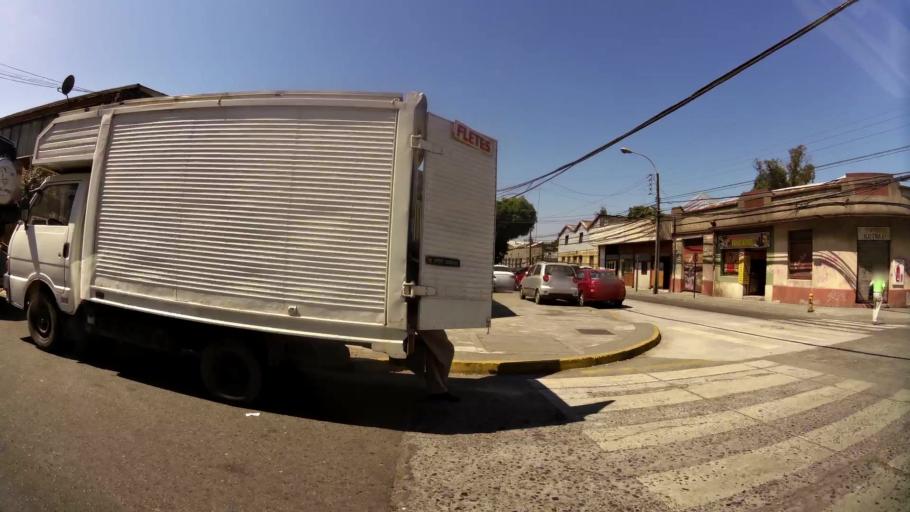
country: CL
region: Biobio
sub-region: Provincia de Concepcion
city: Concepcion
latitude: -36.8217
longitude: -73.0513
